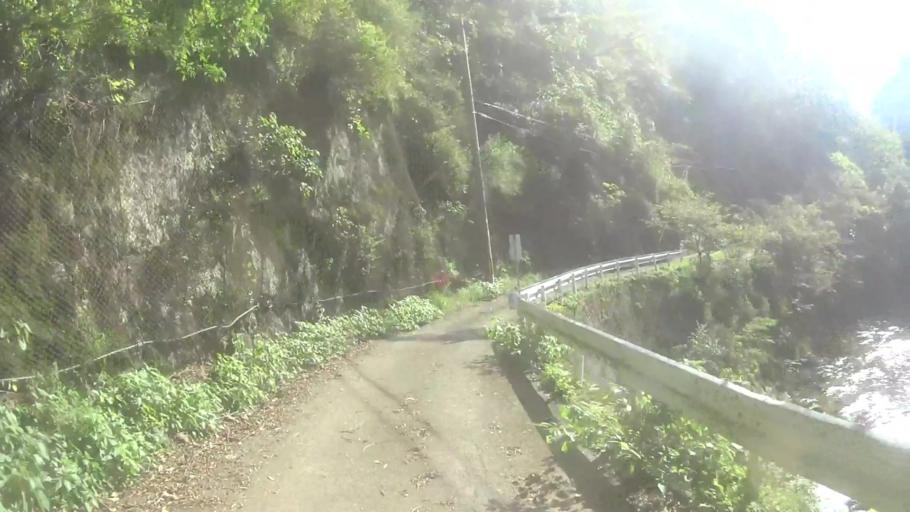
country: JP
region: Kyoto
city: Miyazu
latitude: 35.7197
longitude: 135.1646
